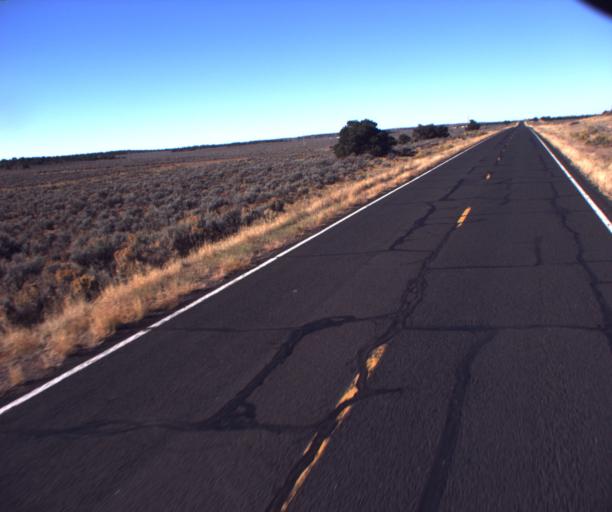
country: US
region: Arizona
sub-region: Navajo County
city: First Mesa
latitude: 35.7391
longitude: -110.0796
